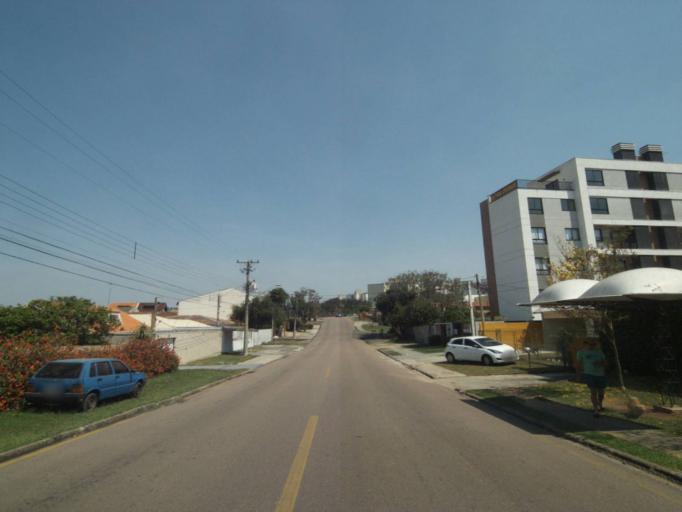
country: BR
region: Parana
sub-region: Curitiba
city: Curitiba
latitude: -25.4792
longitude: -49.2858
